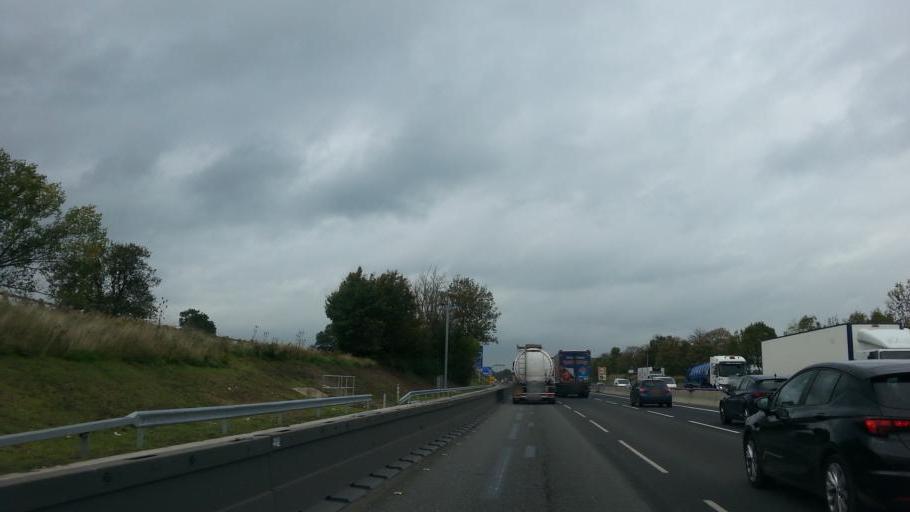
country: GB
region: England
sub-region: Cheshire East
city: Knutsford
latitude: 53.2895
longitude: -2.3958
